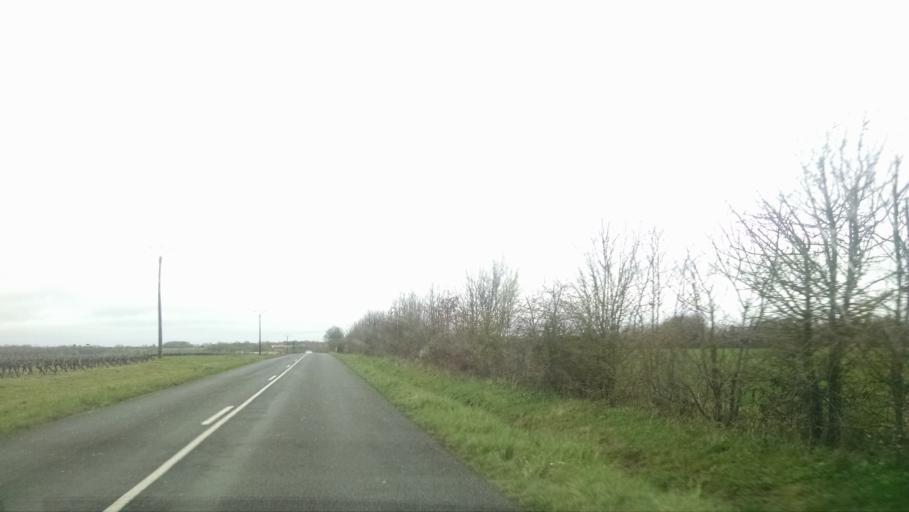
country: FR
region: Pays de la Loire
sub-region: Departement de la Loire-Atlantique
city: Maisdon-sur-Sevre
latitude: 47.0870
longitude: -1.3887
